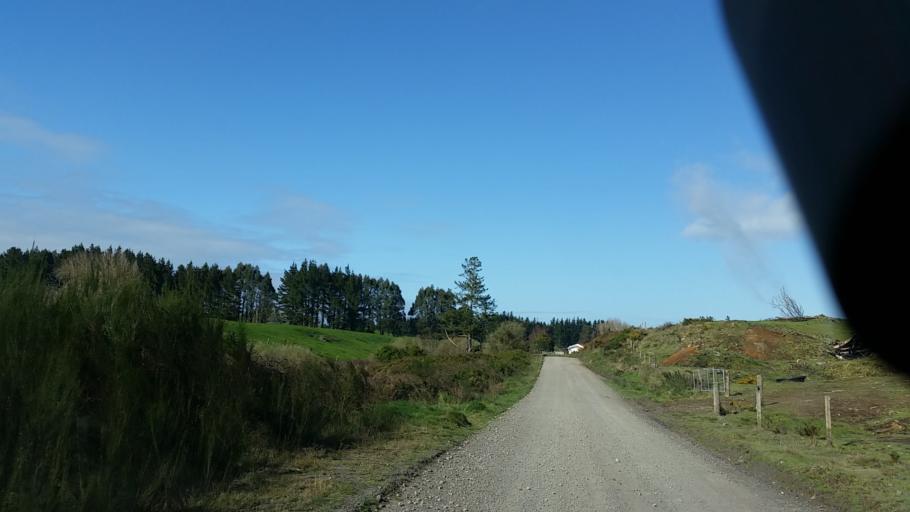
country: NZ
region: Bay of Plenty
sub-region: Rotorua District
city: Rotorua
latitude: -38.2626
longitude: 176.1596
